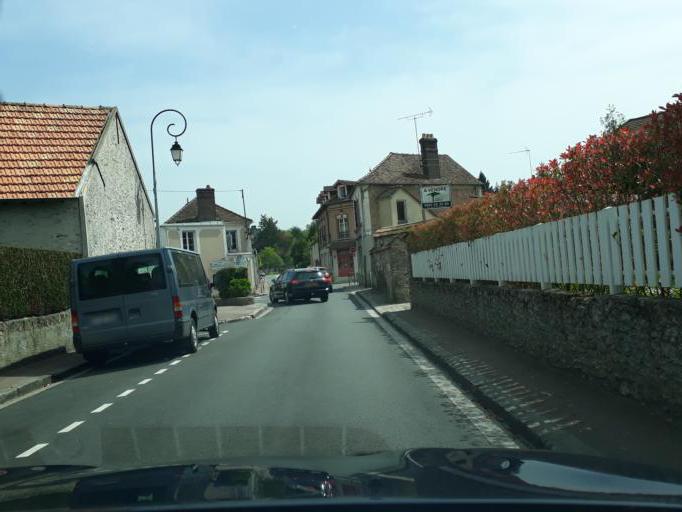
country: FR
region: Ile-de-France
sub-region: Departement des Yvelines
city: Saint-Leger-en-Yvelines
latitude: 48.7211
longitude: 1.7660
